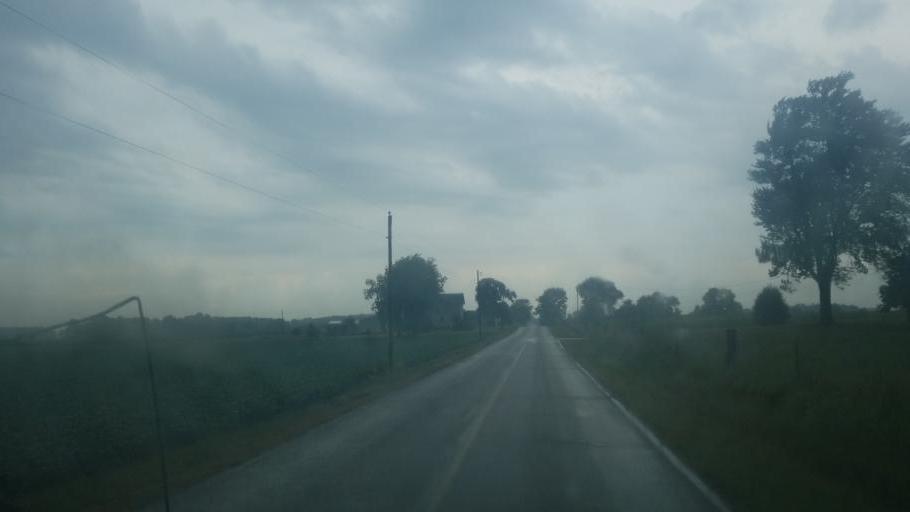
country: US
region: Indiana
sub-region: DeKalb County
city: Butler
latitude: 41.4732
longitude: -84.8502
